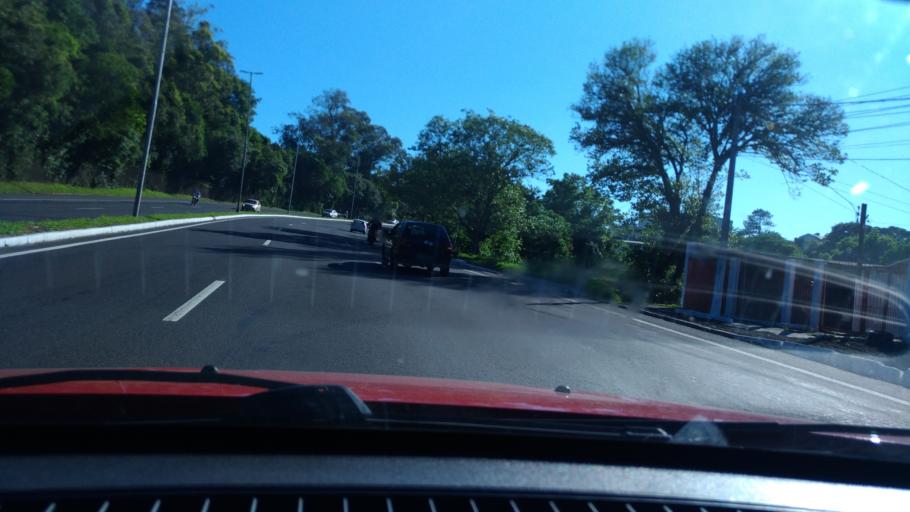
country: BR
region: Rio Grande do Sul
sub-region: Viamao
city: Viamao
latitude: -30.0797
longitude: -51.1112
